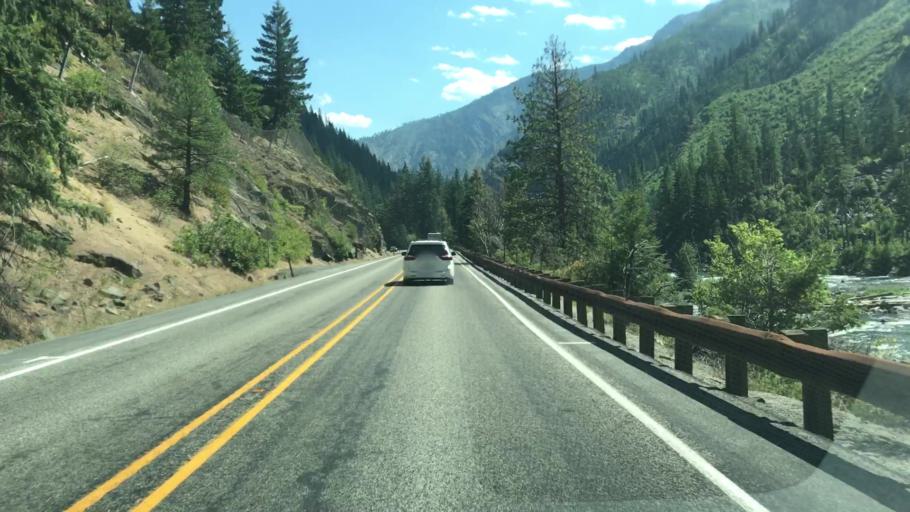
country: US
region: Washington
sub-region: Chelan County
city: Leavenworth
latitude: 47.6298
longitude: -120.7276
